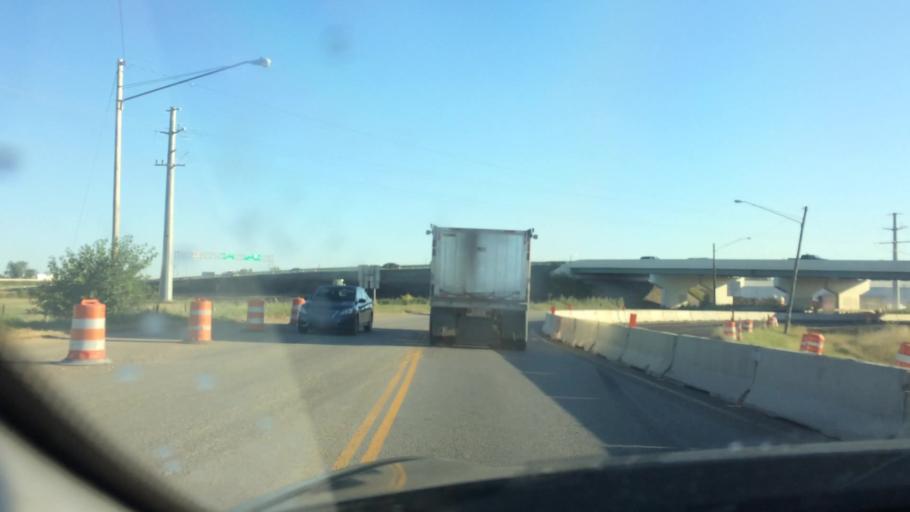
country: US
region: Ohio
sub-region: Hancock County
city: Findlay
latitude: 41.0229
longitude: -83.6689
